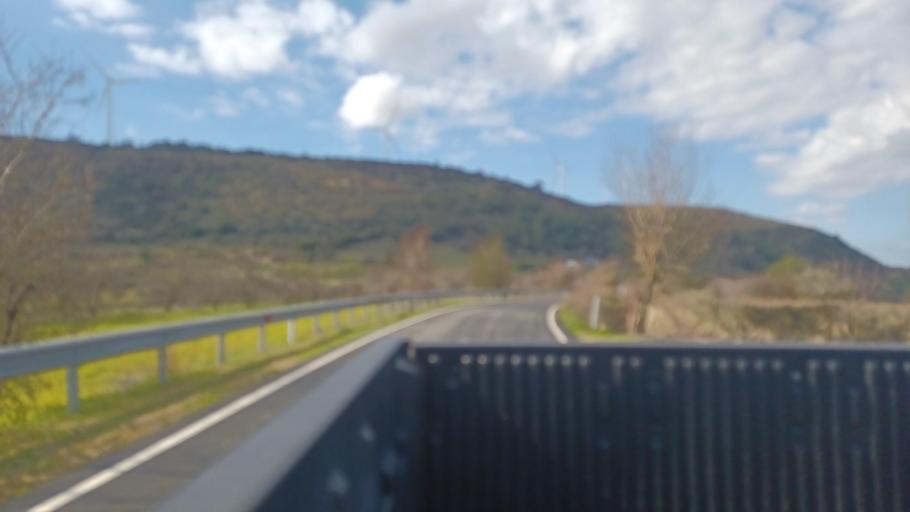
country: CY
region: Limassol
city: Pissouri
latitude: 34.7472
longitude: 32.6680
